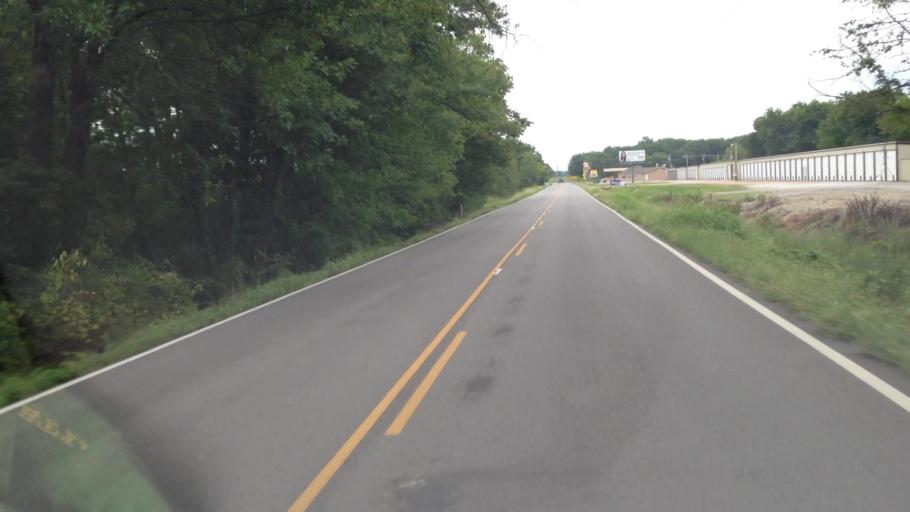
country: US
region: Oklahoma
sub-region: Delaware County
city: Cleora
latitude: 36.5694
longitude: -94.9743
